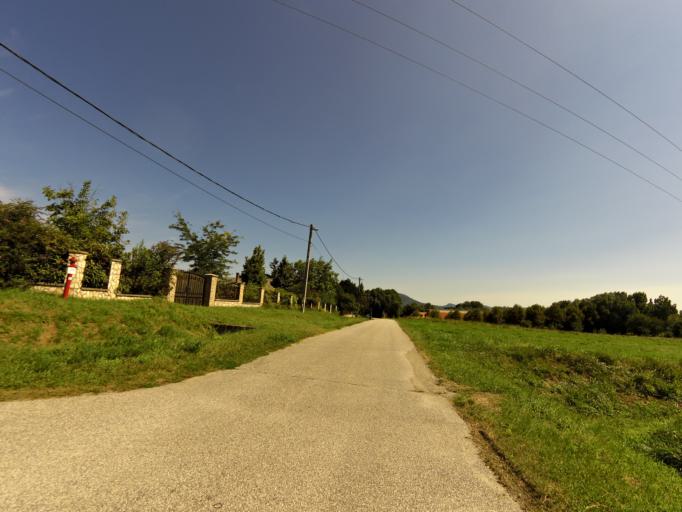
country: HU
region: Veszprem
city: Tapolca
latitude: 46.8264
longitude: 17.3713
